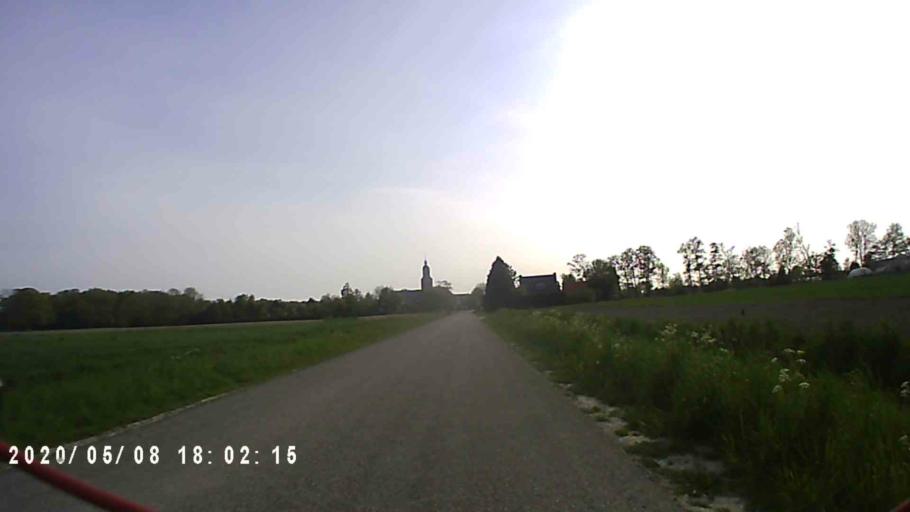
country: NL
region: Groningen
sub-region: Gemeente Winsum
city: Winsum
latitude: 53.3686
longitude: 6.4647
